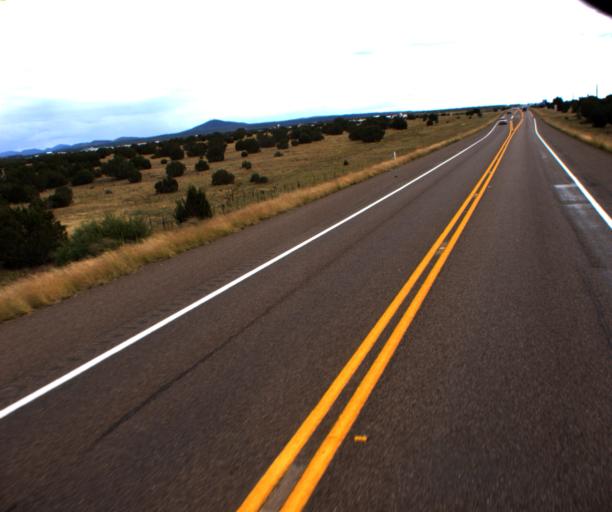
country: US
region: Arizona
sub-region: Navajo County
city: Show Low
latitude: 34.2717
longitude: -110.0238
